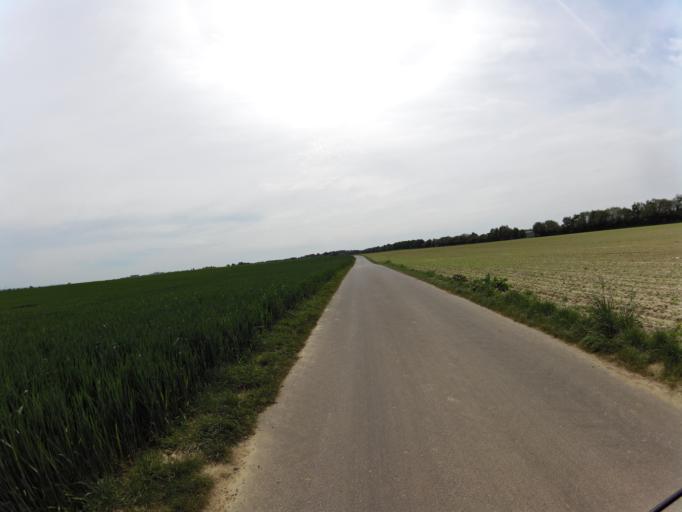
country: DE
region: North Rhine-Westphalia
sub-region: Regierungsbezirk Koln
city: Wurselen
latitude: 50.8373
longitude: 6.1489
